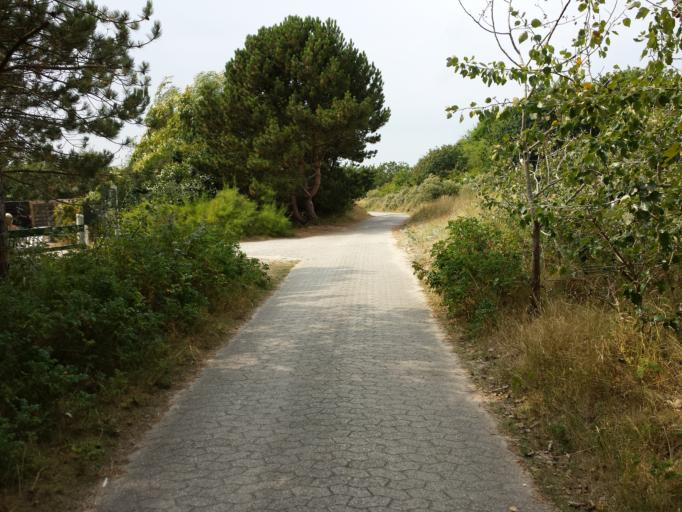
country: DE
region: Lower Saxony
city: Spiekeroog
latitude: 53.7746
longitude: 7.7156
